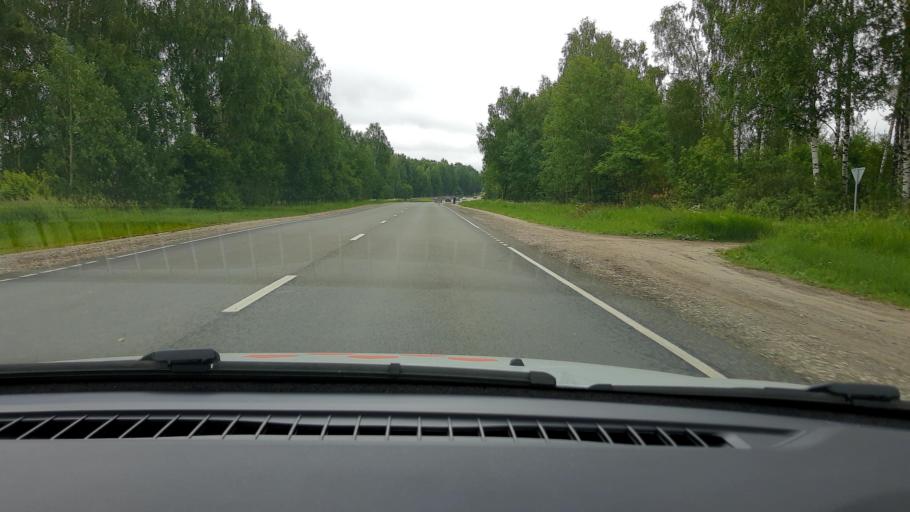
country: RU
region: Nizjnij Novgorod
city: Linda
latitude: 56.6207
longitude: 44.0745
